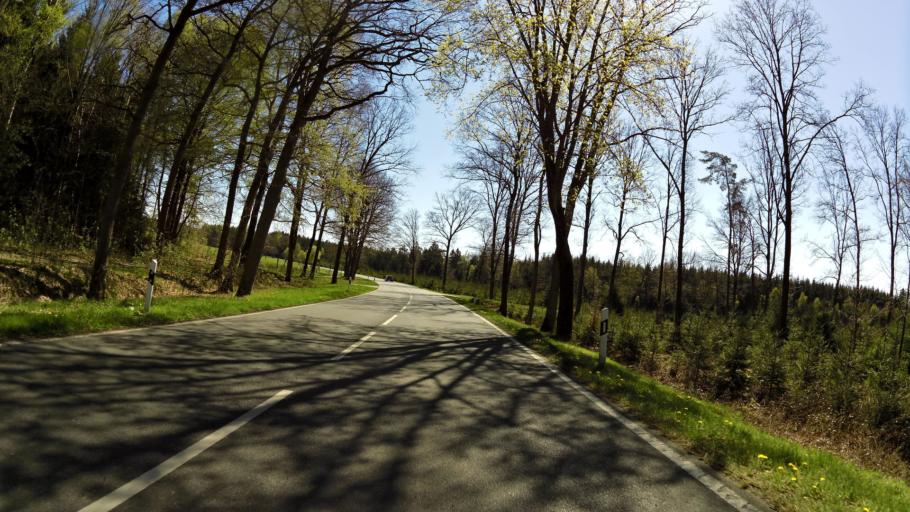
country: DE
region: Lower Saxony
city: Soltau
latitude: 53.0141
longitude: 9.7788
